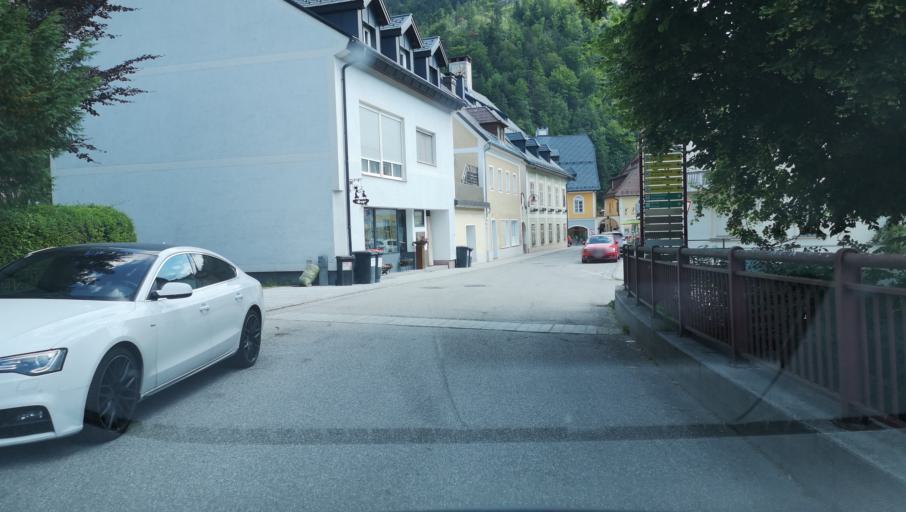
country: AT
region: Lower Austria
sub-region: Politischer Bezirk Amstetten
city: Hollenstein an der Ybbs
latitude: 47.8026
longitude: 14.7716
